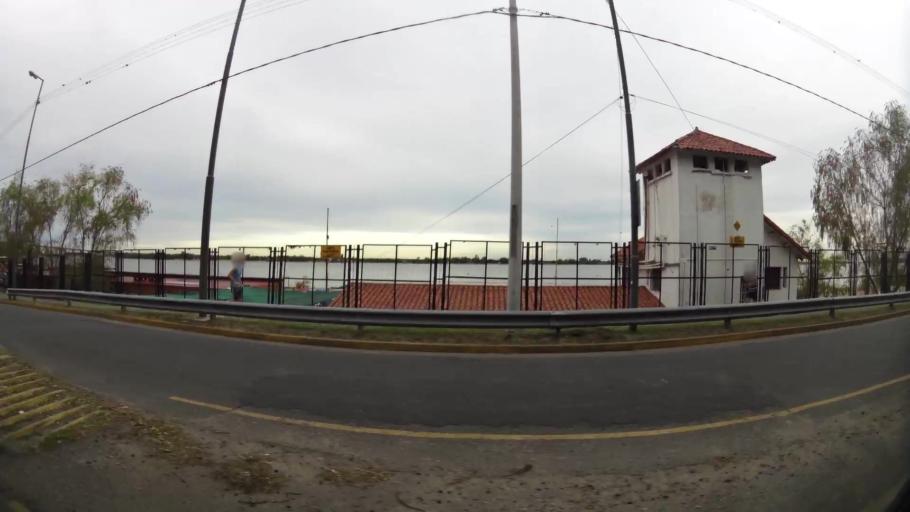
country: AR
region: Santa Fe
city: Granadero Baigorria
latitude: -32.8829
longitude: -60.6880
